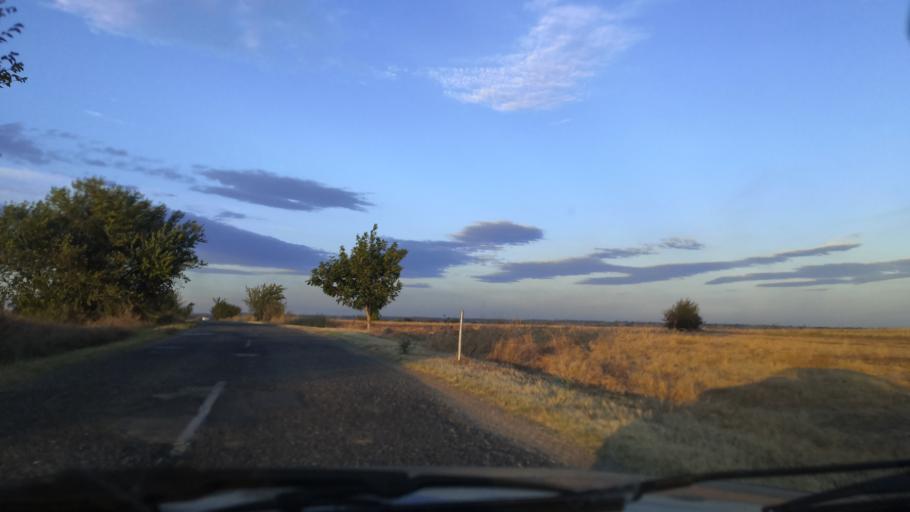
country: RO
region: Mehedinti
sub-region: Comuna Gruia
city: Izvoarele
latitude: 44.2573
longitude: 22.6330
